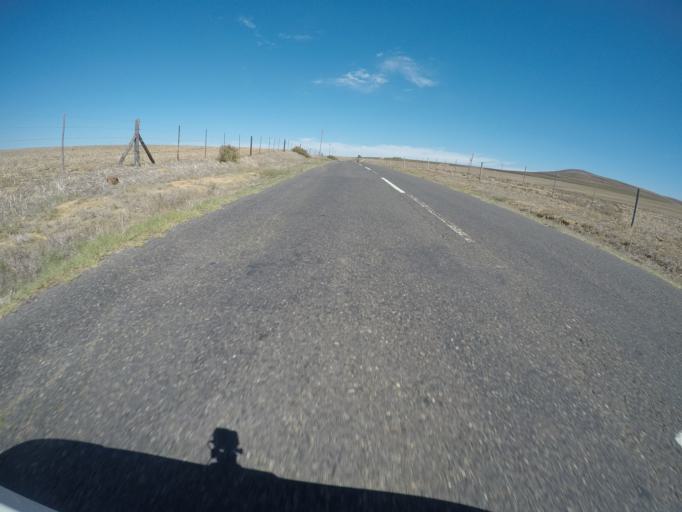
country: ZA
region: Western Cape
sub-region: City of Cape Town
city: Atlantis
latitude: -33.7032
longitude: 18.5870
